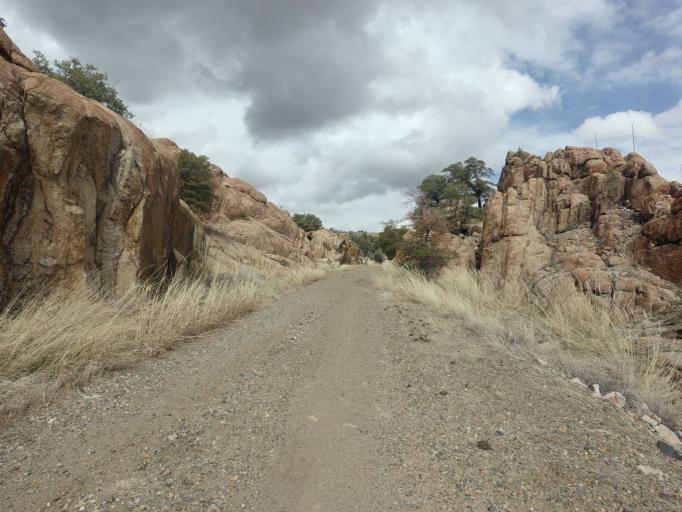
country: US
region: Arizona
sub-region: Yavapai County
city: Prescott Valley
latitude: 34.6073
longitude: -112.3901
